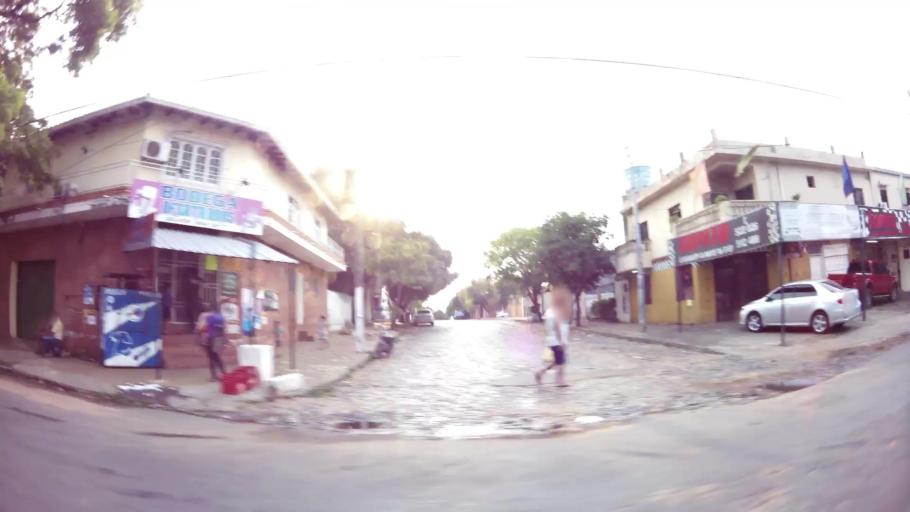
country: PY
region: Central
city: Lambare
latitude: -25.3273
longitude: -57.5750
